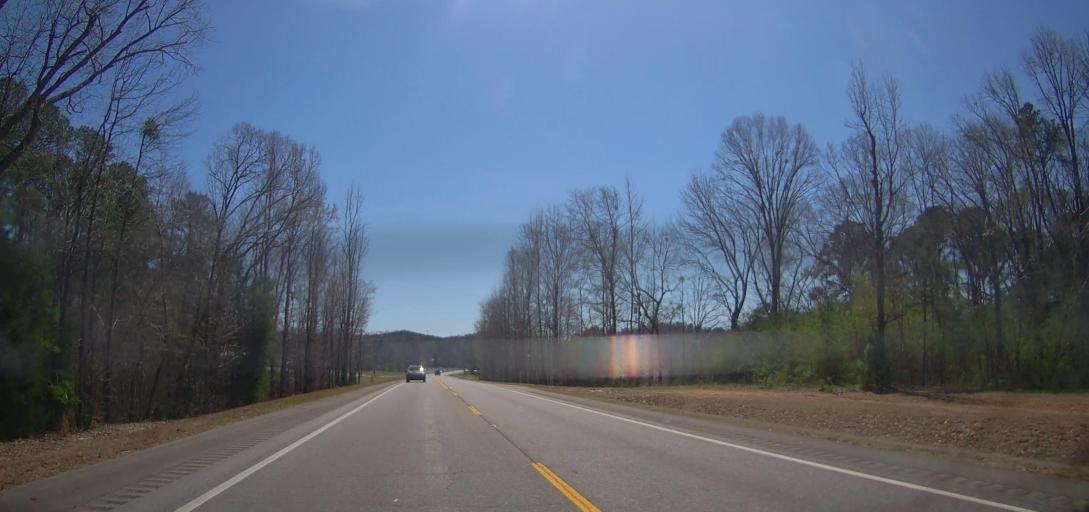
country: US
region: Alabama
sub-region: Calhoun County
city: Ohatchee
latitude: 33.8199
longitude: -86.0396
